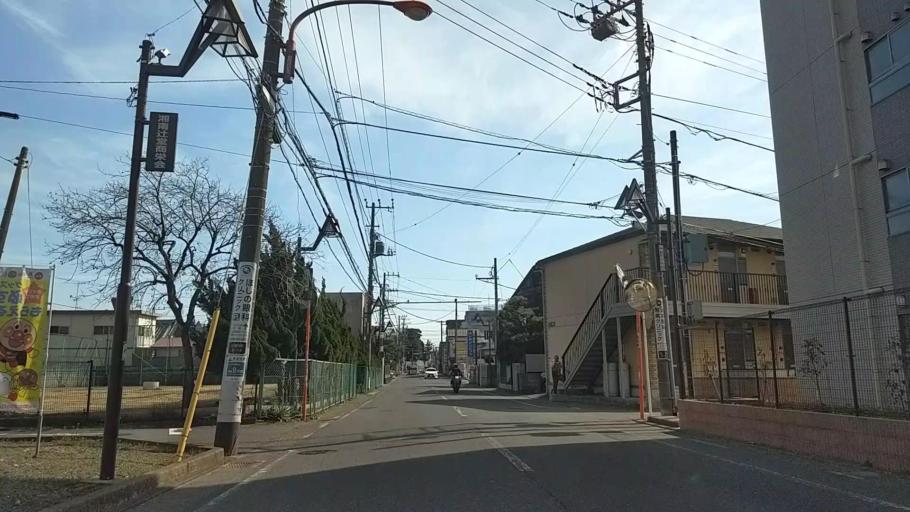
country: JP
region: Kanagawa
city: Fujisawa
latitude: 35.3291
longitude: 139.4522
